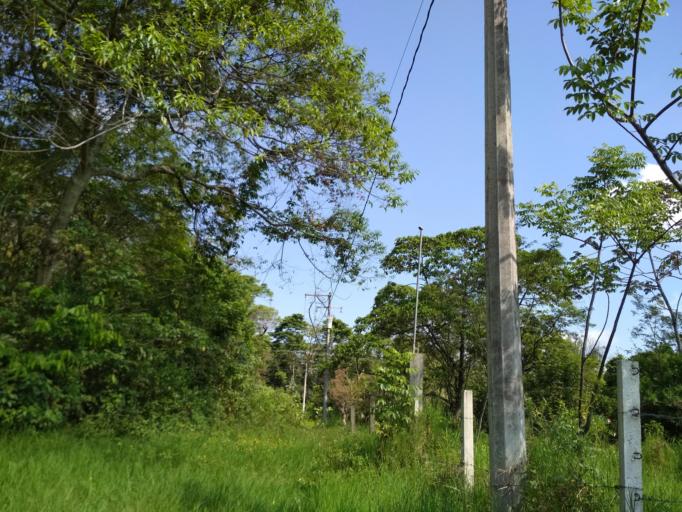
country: MX
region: Veracruz
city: Cordoba
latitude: 18.8739
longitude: -96.9082
